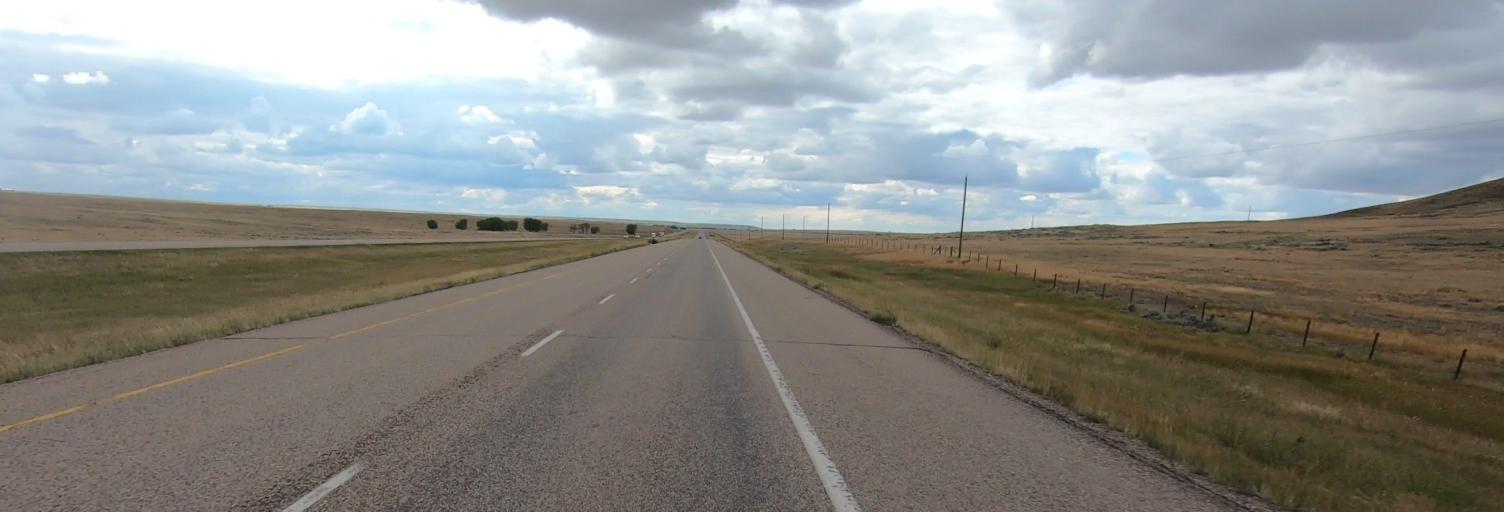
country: CA
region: Alberta
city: Medicine Hat
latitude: 49.9402
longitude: -110.0905
